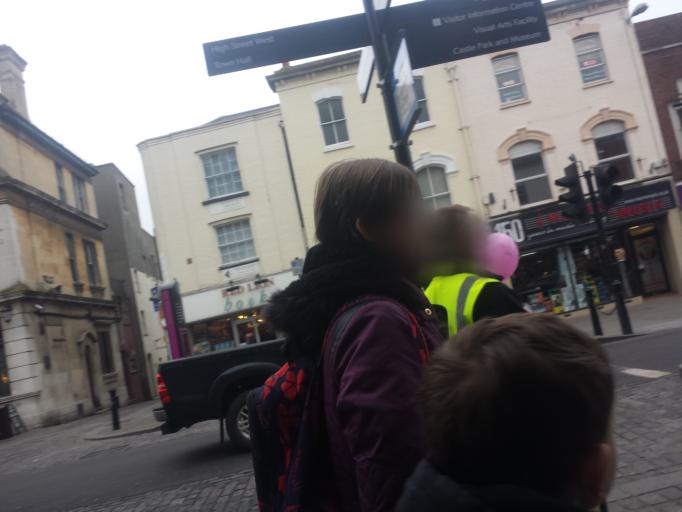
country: GB
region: England
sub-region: Essex
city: Colchester
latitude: 51.8894
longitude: 0.9004
